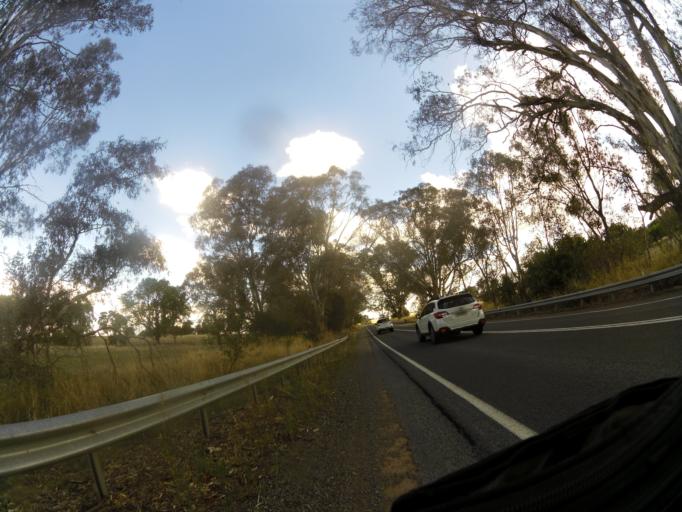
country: AU
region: Victoria
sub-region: Mansfield
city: Mansfield
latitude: -36.9389
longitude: 145.9988
